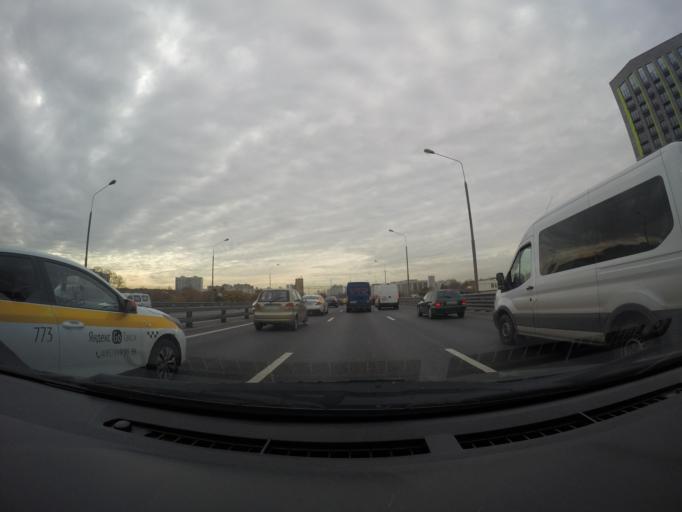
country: RU
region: Moscow
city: Vatutino
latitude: 55.8606
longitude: 37.6911
